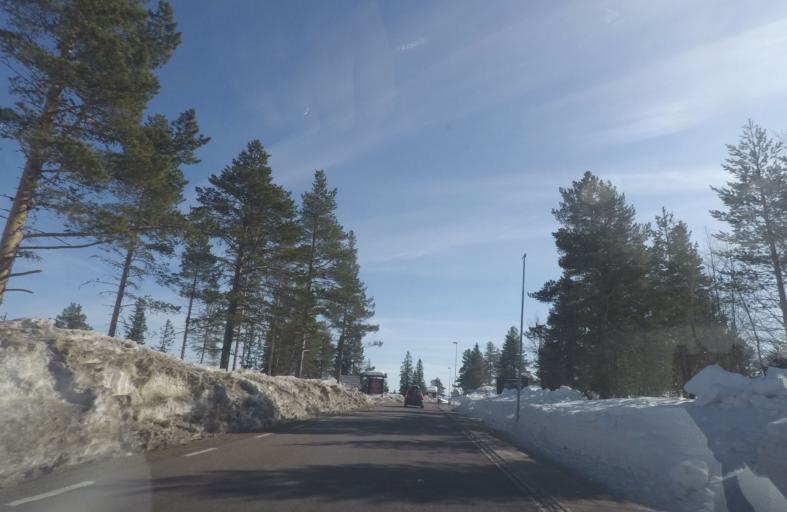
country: SE
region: Dalarna
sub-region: Malung-Saelens kommun
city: Malung
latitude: 61.1671
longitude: 13.1710
